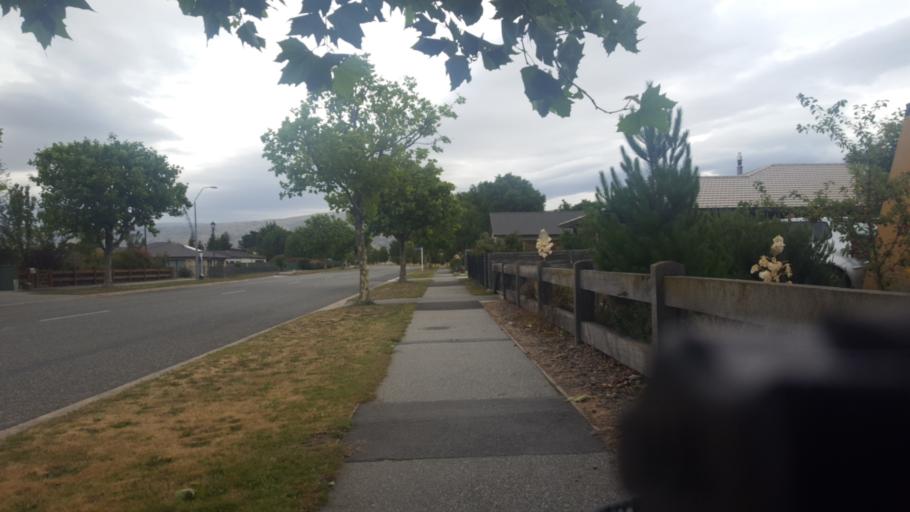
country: NZ
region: Otago
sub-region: Queenstown-Lakes District
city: Wanaka
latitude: -45.0466
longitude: 169.1866
